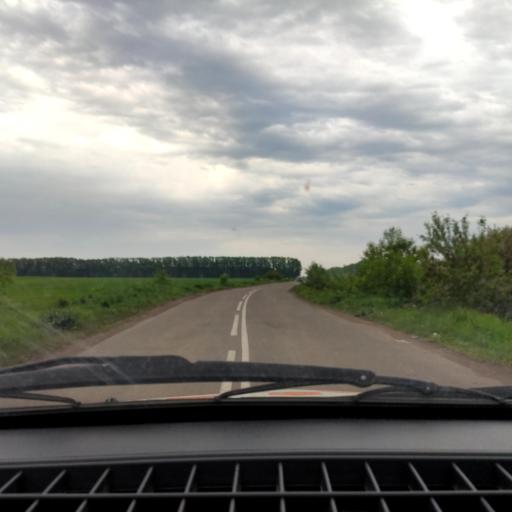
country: RU
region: Bashkortostan
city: Avdon
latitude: 54.5394
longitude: 55.7619
